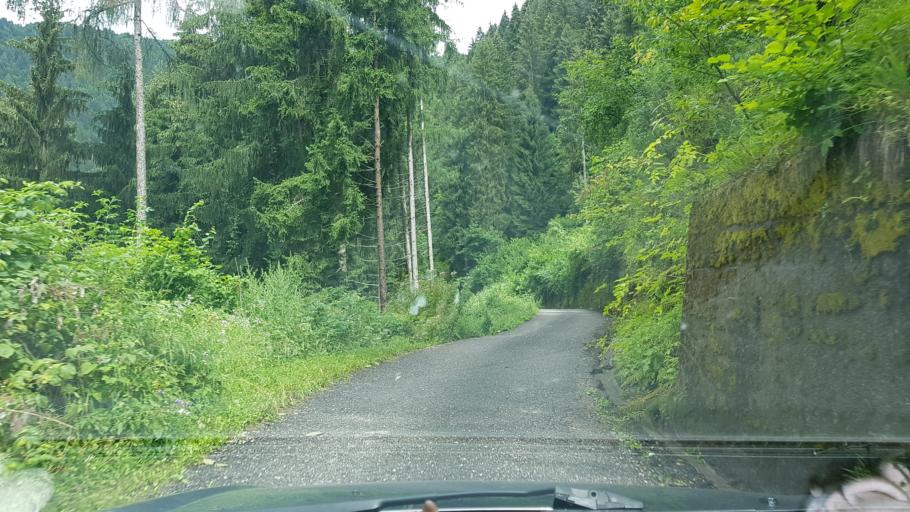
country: IT
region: Friuli Venezia Giulia
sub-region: Provincia di Udine
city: Cercivento
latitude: 46.5341
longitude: 12.9831
